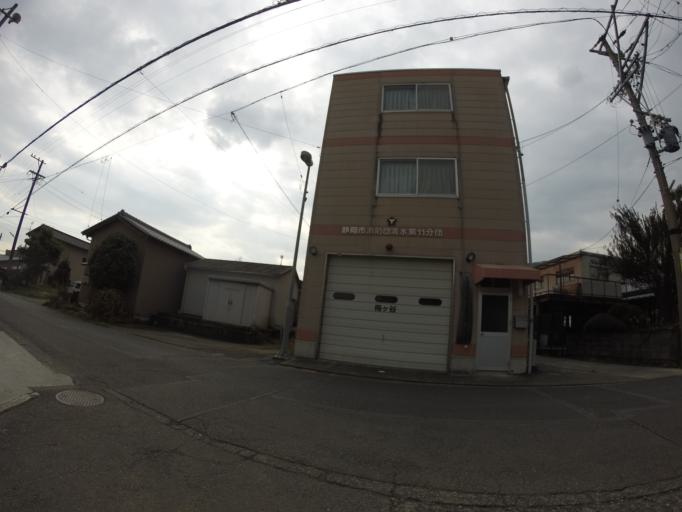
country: JP
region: Shizuoka
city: Shizuoka-shi
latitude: 35.0440
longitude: 138.4505
